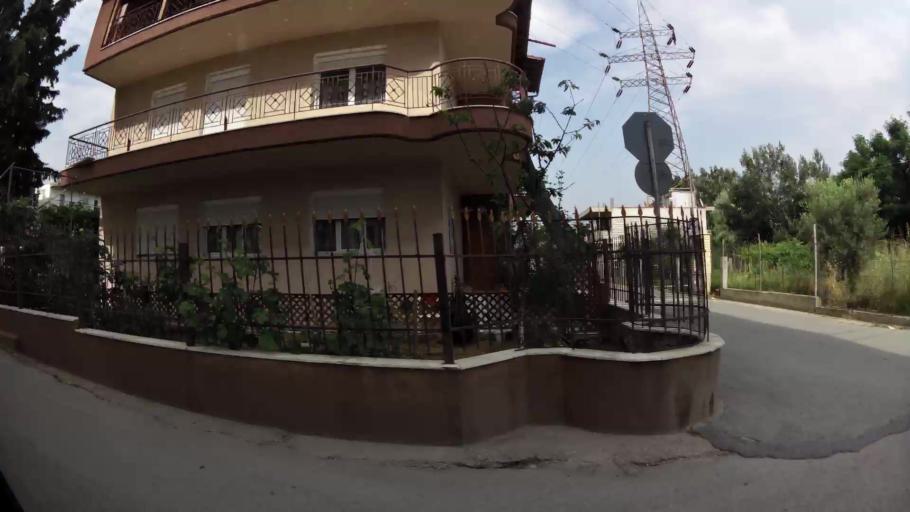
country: GR
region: Central Macedonia
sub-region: Nomos Thessalonikis
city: Stavroupoli
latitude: 40.6889
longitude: 22.9297
